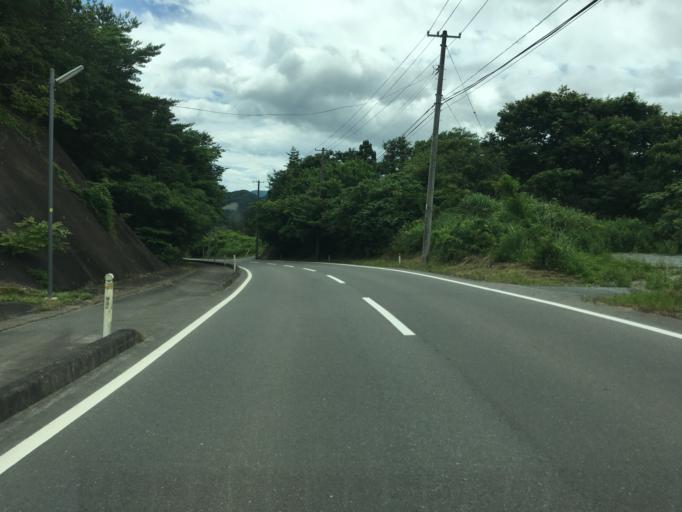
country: JP
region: Miyagi
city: Marumori
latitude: 37.7399
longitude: 140.9275
